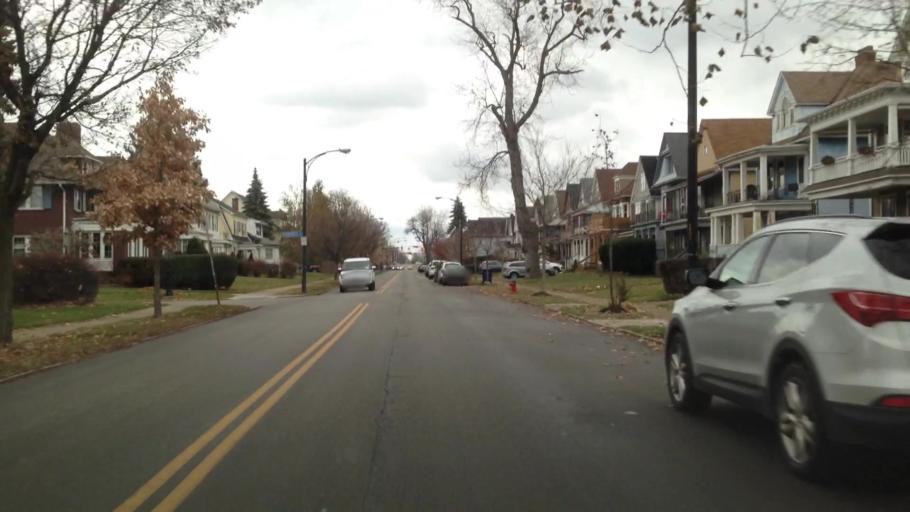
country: US
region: New York
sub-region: Erie County
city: Kenmore
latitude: 42.9403
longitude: -78.8423
